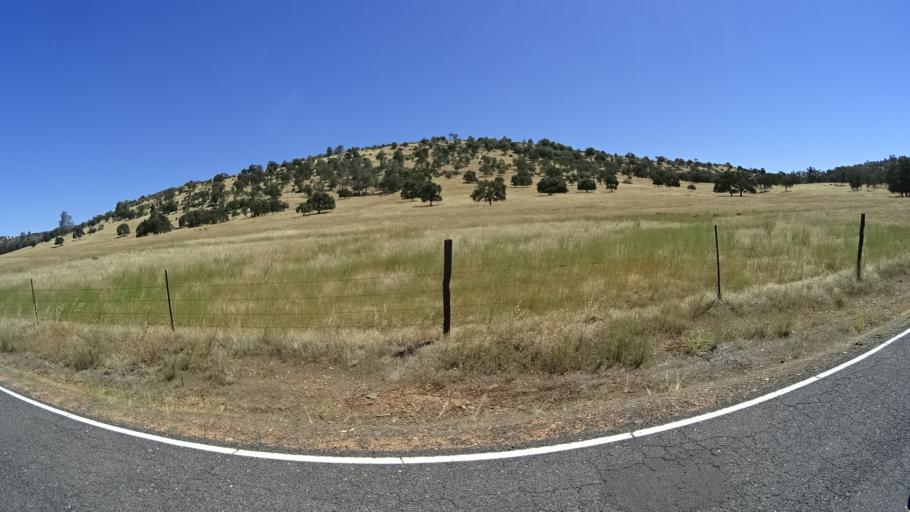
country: US
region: California
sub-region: Calaveras County
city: Copperopolis
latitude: 38.0131
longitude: -120.6738
